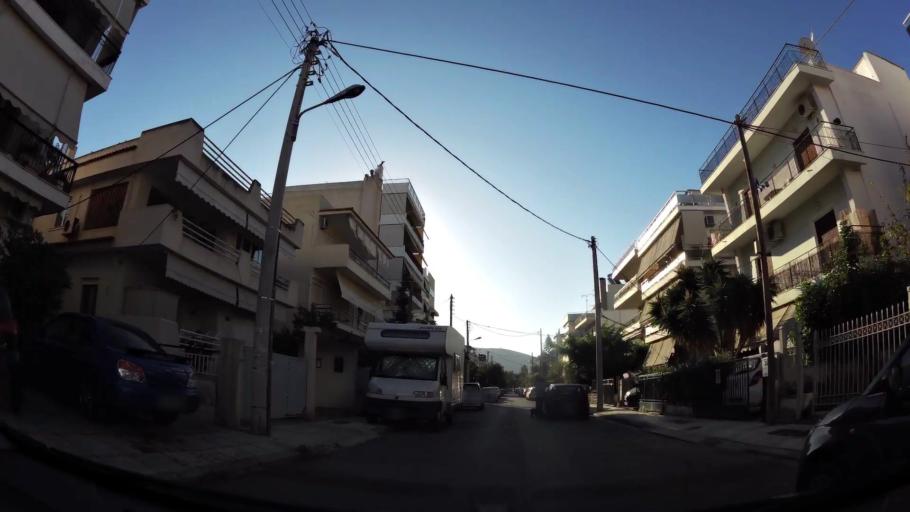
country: GR
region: Attica
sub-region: Nomarchia Athinas
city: Argyroupoli
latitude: 37.8873
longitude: 23.7573
